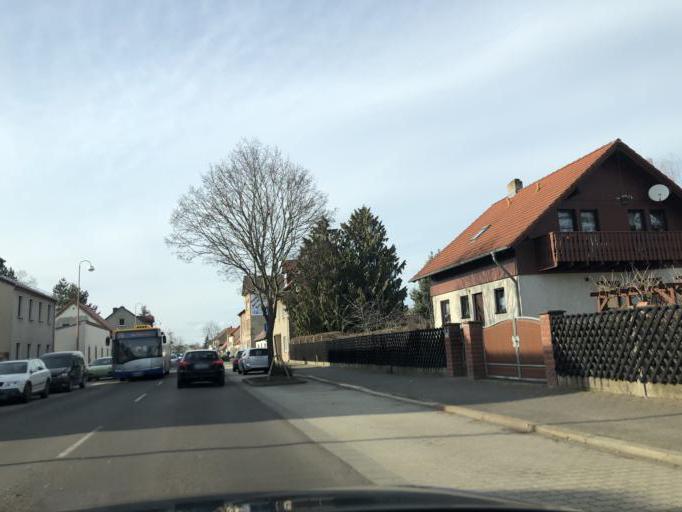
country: DE
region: Saxony
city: Grossposna
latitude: 51.2796
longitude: 12.4655
